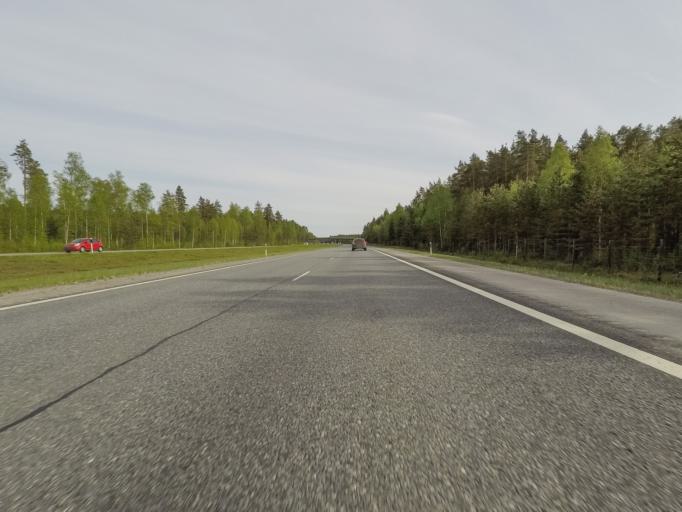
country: FI
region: Haeme
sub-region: Haemeenlinna
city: Janakkala
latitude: 60.9289
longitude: 24.5203
